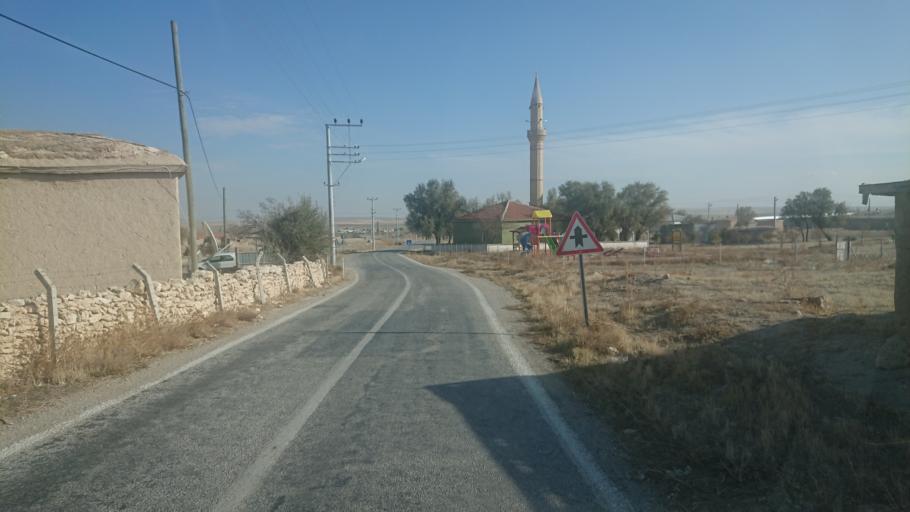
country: TR
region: Aksaray
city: Sultanhani
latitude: 38.0400
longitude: 33.5938
